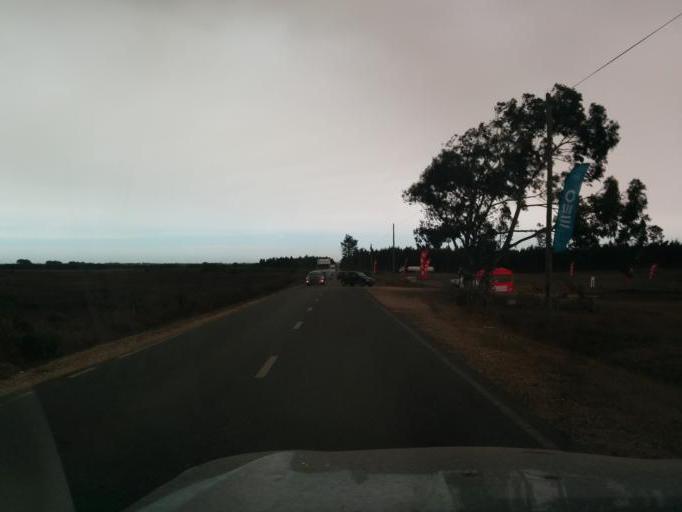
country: PT
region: Beja
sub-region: Odemira
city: Sao Teotonio
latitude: 37.5549
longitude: -8.7349
